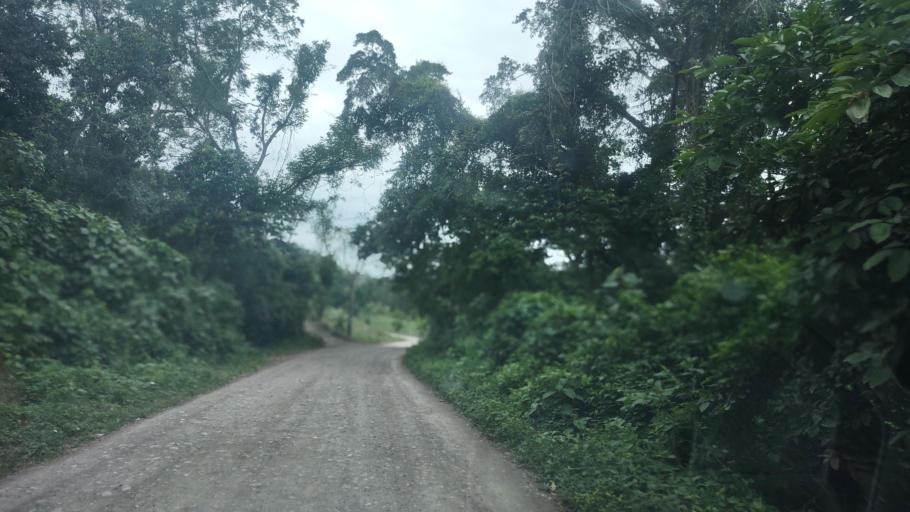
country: MX
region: Veracruz
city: Papantla de Olarte
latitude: 20.4222
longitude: -97.2675
